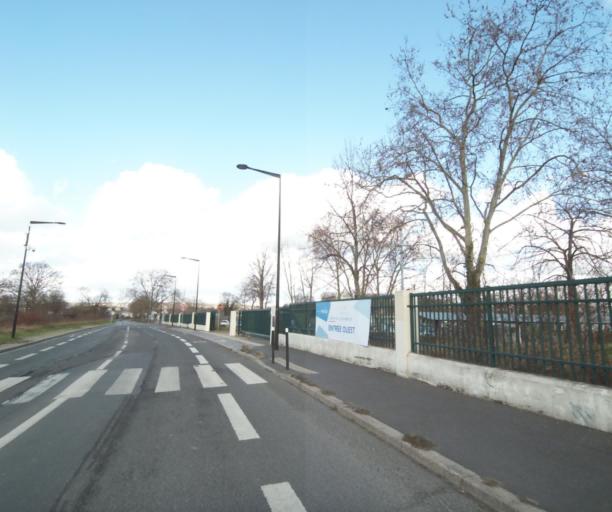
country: FR
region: Ile-de-France
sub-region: Departement de Seine-Saint-Denis
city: Villetaneuse
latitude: 48.9558
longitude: 2.3388
